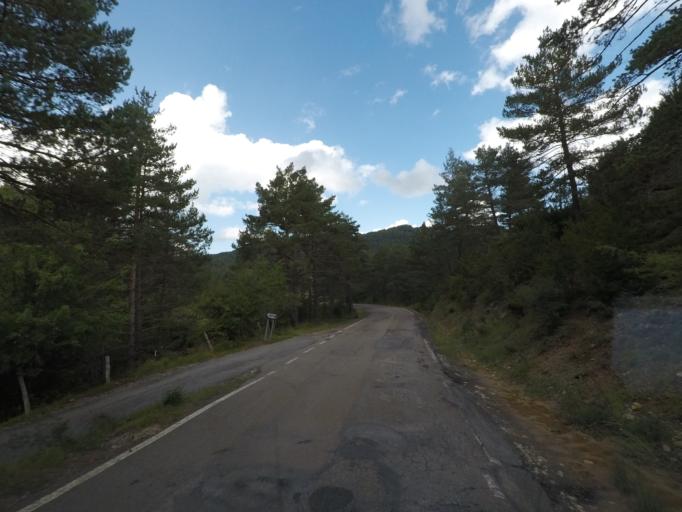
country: ES
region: Aragon
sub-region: Provincia de Huesca
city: Fiscal
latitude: 42.4030
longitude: -0.0778
